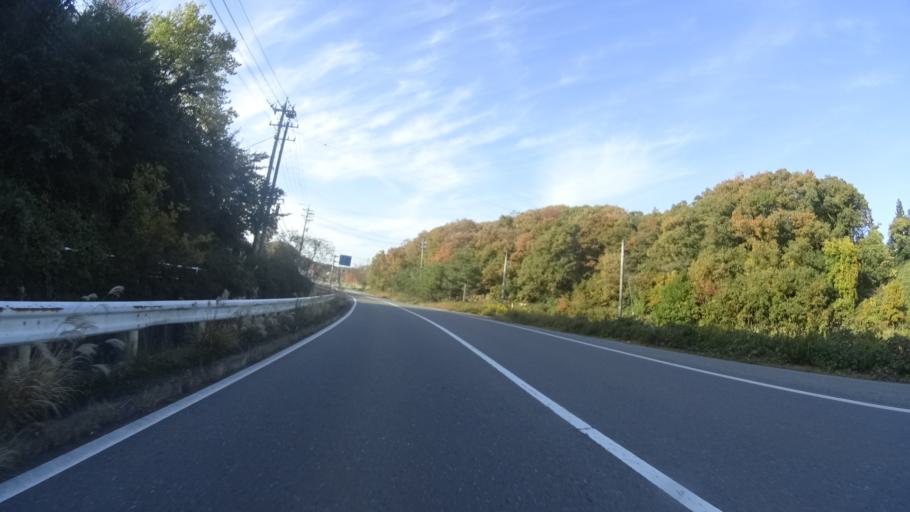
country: JP
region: Ishikawa
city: Hakui
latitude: 37.0239
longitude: 136.7855
